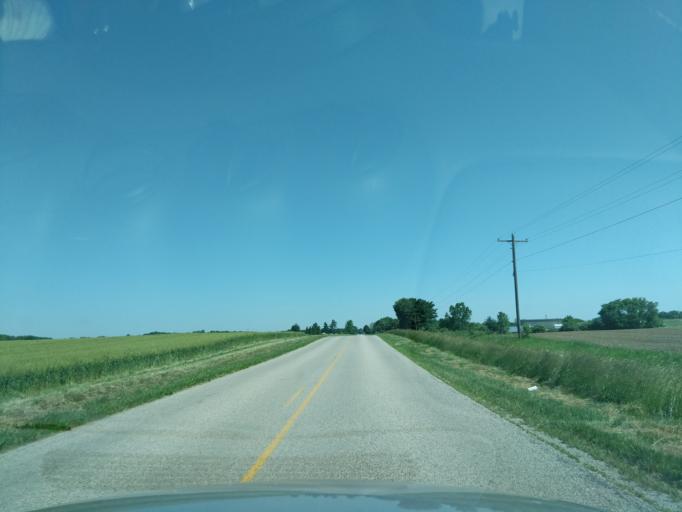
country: US
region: Indiana
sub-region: Huntington County
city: Huntington
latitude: 40.8185
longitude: -85.5083
